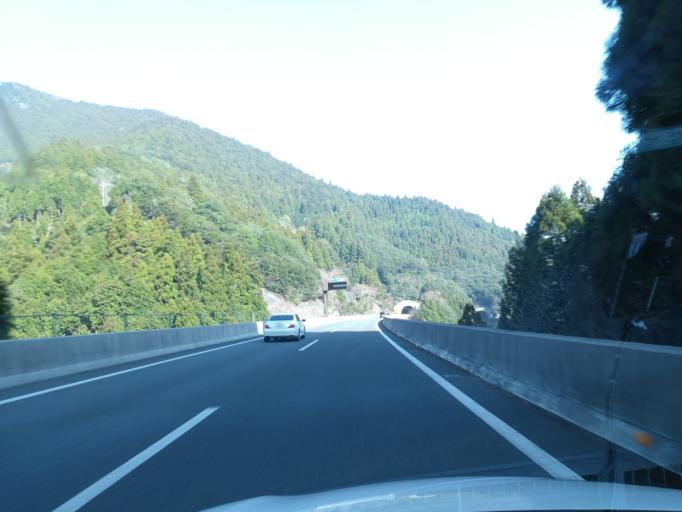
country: JP
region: Ehime
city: Kawanoecho
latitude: 33.8332
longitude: 133.6555
